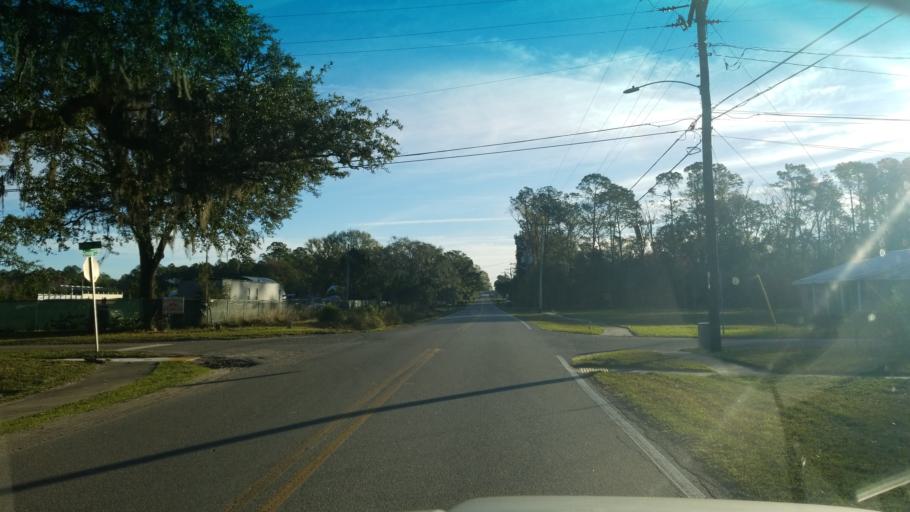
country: US
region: Florida
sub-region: Duval County
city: Baldwin
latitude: 30.3126
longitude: -81.8447
